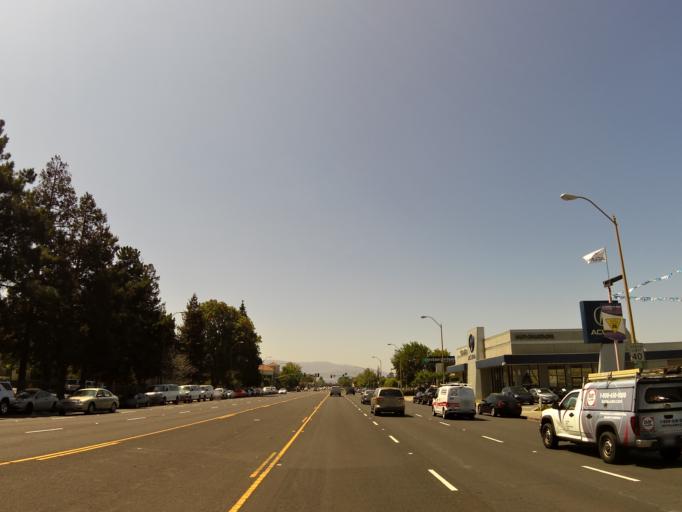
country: US
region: California
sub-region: Santa Clara County
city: Santa Clara
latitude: 37.3232
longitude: -121.9852
